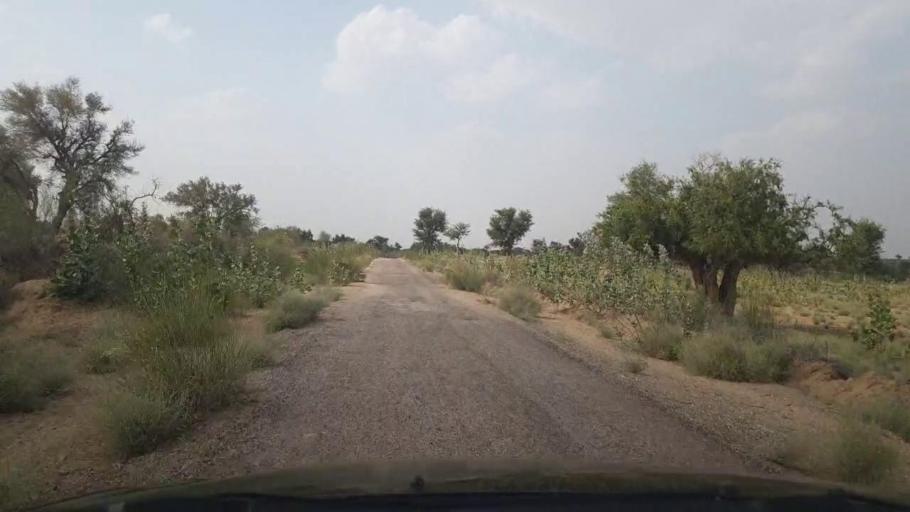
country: PK
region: Sindh
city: Islamkot
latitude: 24.9802
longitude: 70.5829
